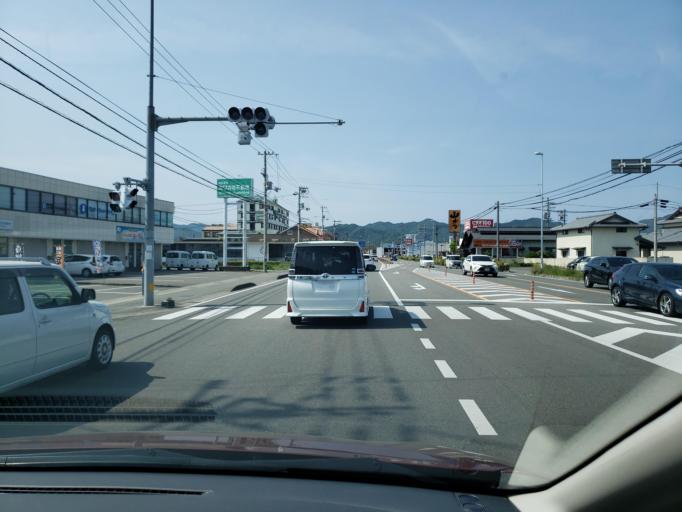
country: JP
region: Tokushima
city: Ishii
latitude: 34.1240
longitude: 134.4774
